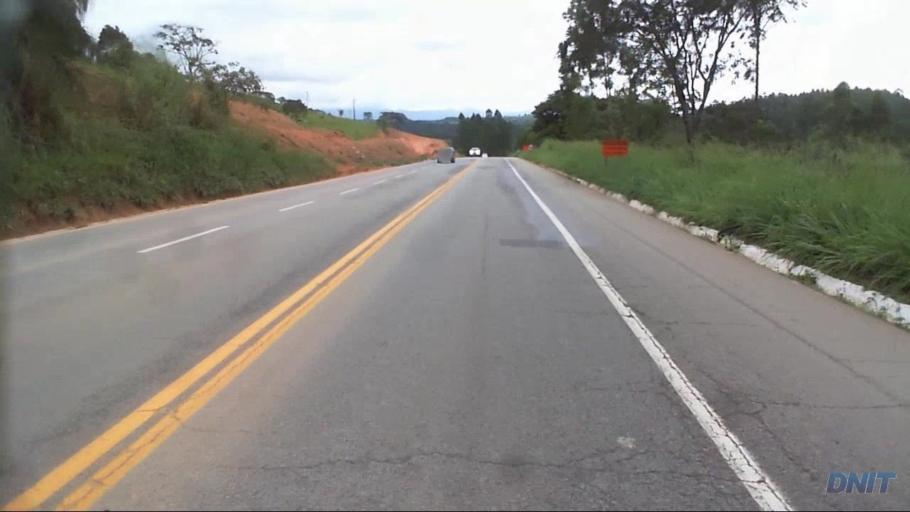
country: BR
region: Minas Gerais
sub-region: Barao De Cocais
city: Barao de Cocais
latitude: -19.7962
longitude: -43.4256
